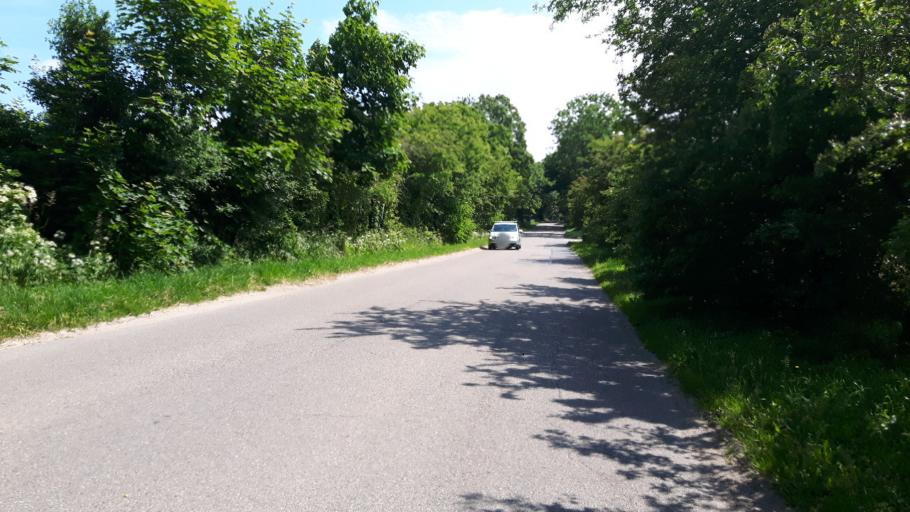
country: PL
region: Pomeranian Voivodeship
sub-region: Powiat wejherowski
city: Choczewo
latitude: 54.7462
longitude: 17.8008
